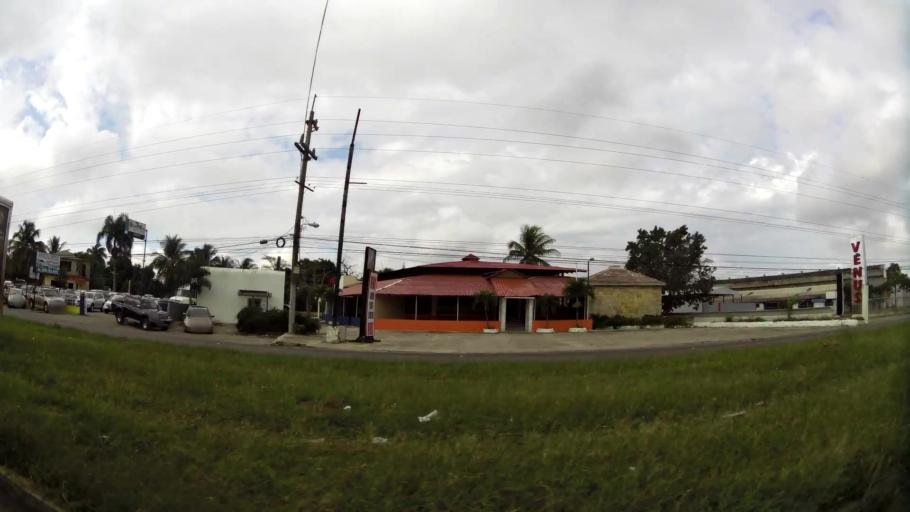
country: DO
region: Santiago
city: Licey al Medio
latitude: 19.4174
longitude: -70.6458
